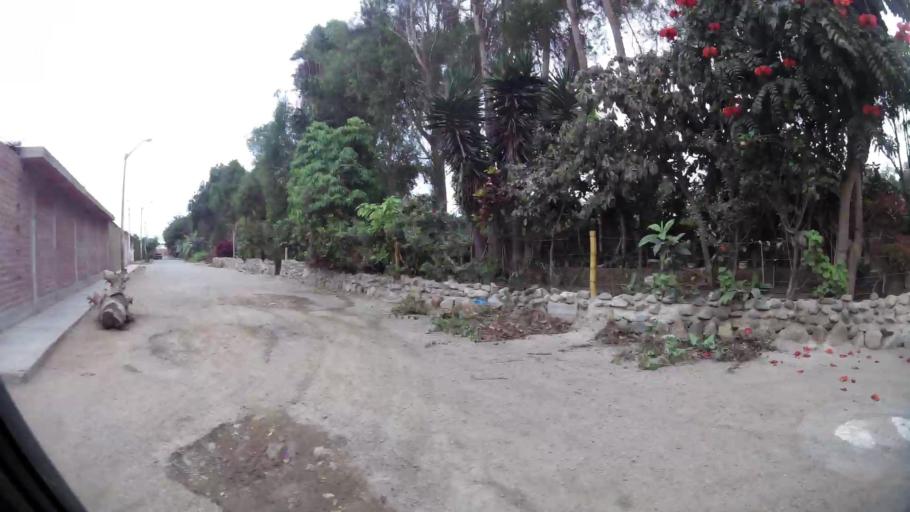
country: PE
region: La Libertad
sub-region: Provincia de Trujillo
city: La Esperanza
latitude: -8.0963
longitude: -79.0640
